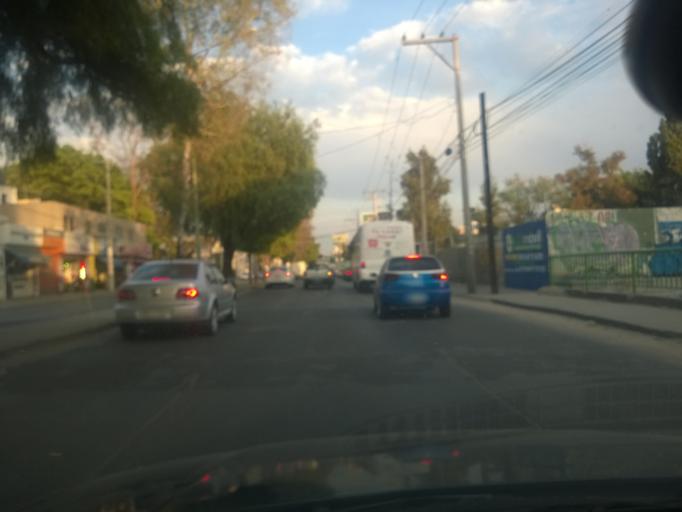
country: MX
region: Guanajuato
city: Leon
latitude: 21.1041
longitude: -101.6419
